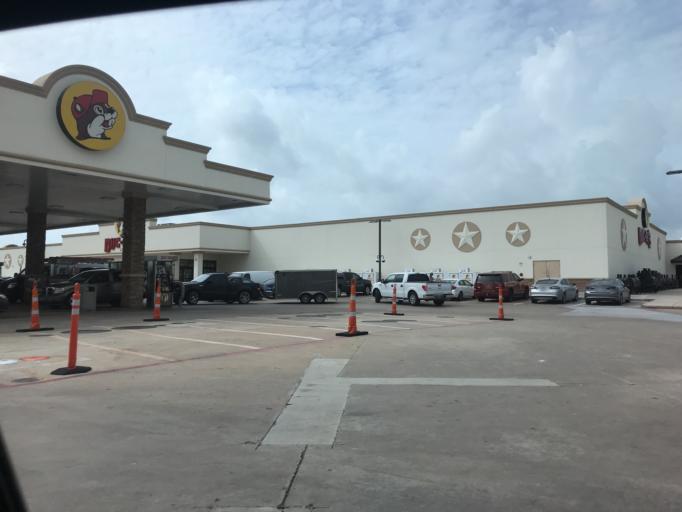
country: US
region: Texas
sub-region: Caldwell County
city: Luling
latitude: 29.6515
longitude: -97.5928
